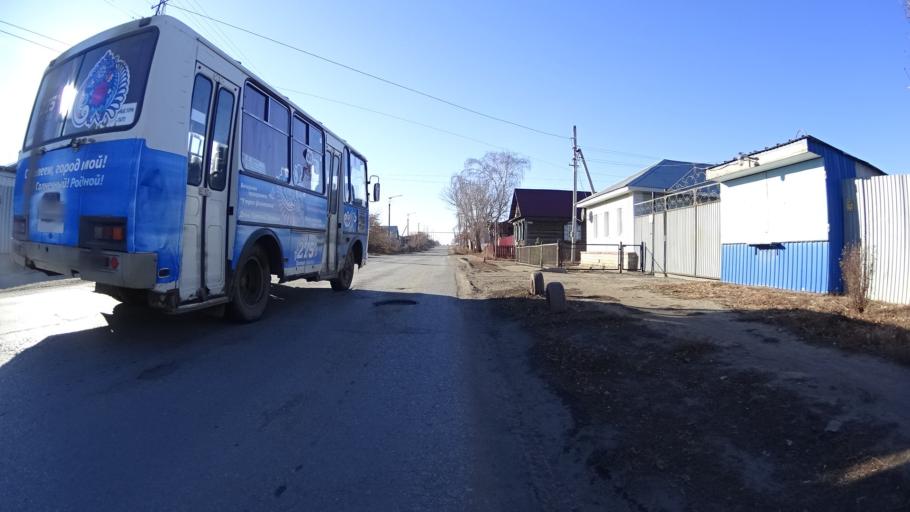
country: RU
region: Chelyabinsk
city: Troitsk
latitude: 54.0874
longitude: 61.5321
